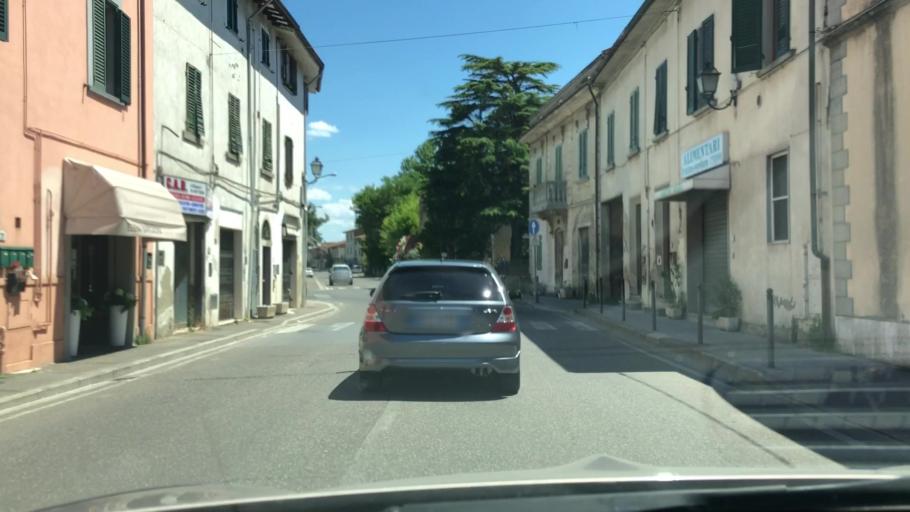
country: IT
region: Tuscany
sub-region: Province of Pisa
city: Ponsacco
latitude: 43.6195
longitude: 10.6345
